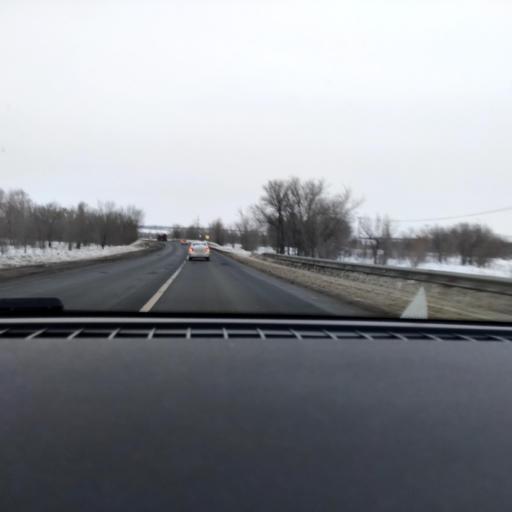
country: RU
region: Samara
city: Dubovyy Umet
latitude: 53.0398
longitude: 50.3497
